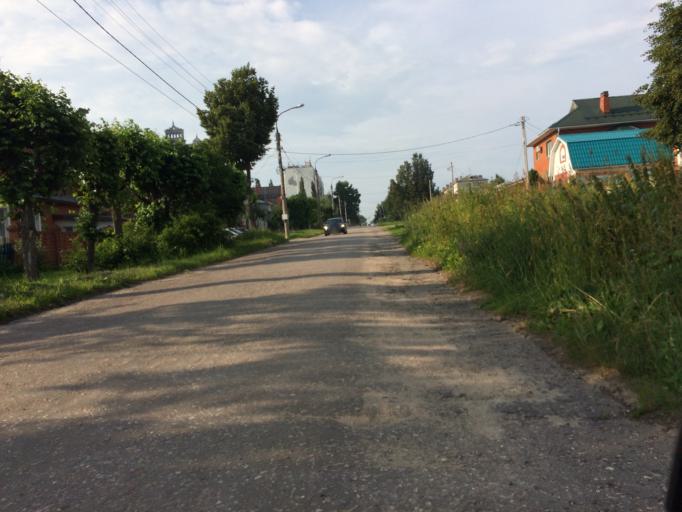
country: RU
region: Mariy-El
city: Yoshkar-Ola
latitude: 56.6196
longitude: 47.9450
